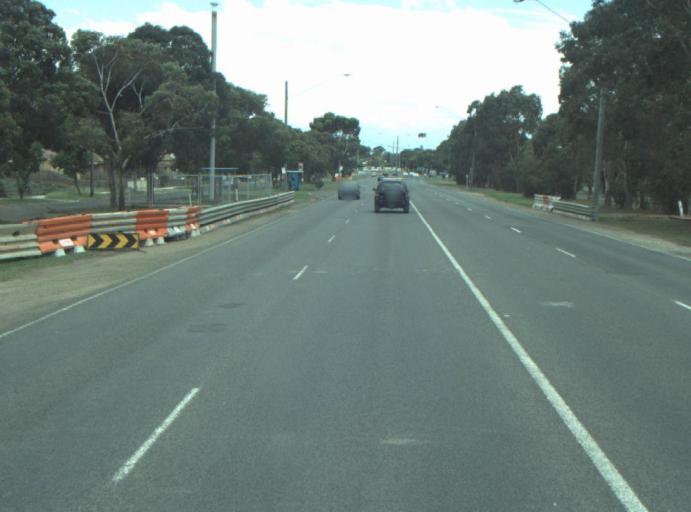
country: AU
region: Victoria
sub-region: Greater Geelong
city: Bell Park
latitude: -38.0800
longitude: 144.3584
